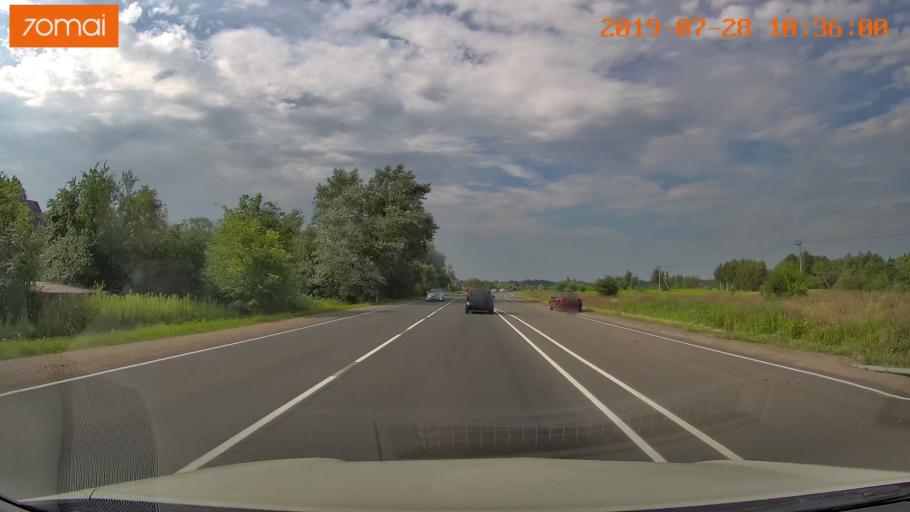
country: RU
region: Kaliningrad
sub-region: Gorod Kaliningrad
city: Kaliningrad
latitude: 54.7413
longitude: 20.4259
